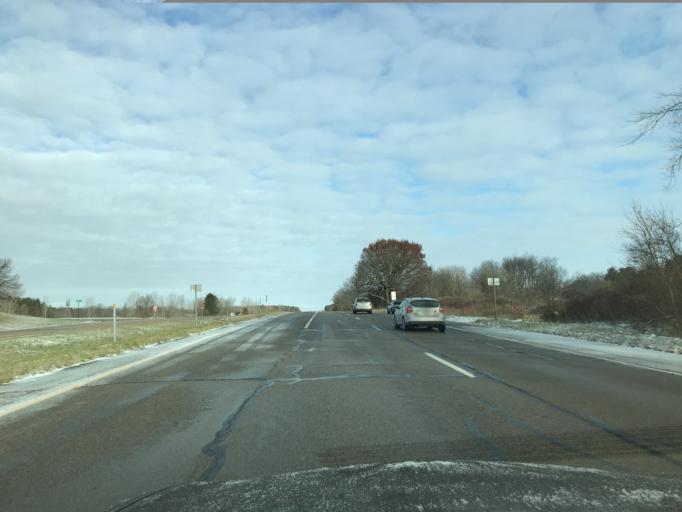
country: US
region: Michigan
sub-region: Eaton County
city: Dimondale
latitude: 42.6251
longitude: -84.6226
